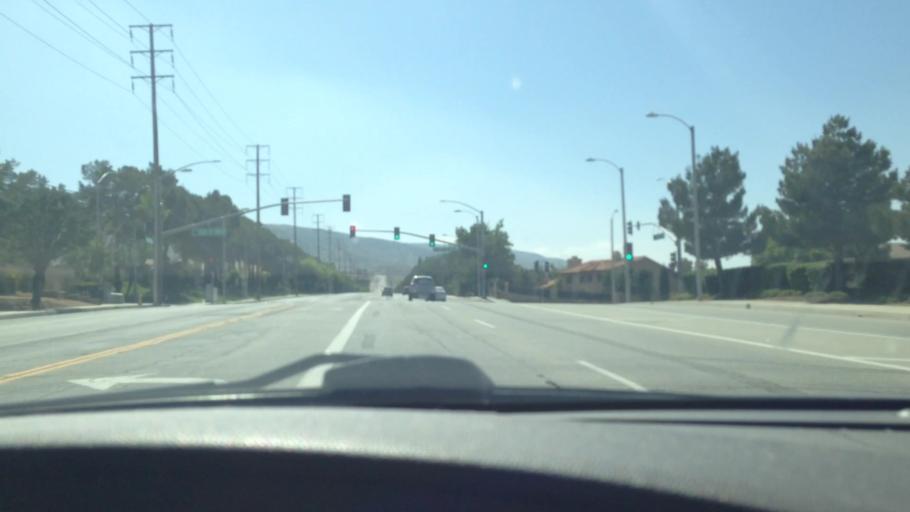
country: US
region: California
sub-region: Los Angeles County
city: Quartz Hill
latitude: 34.6309
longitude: -118.2267
